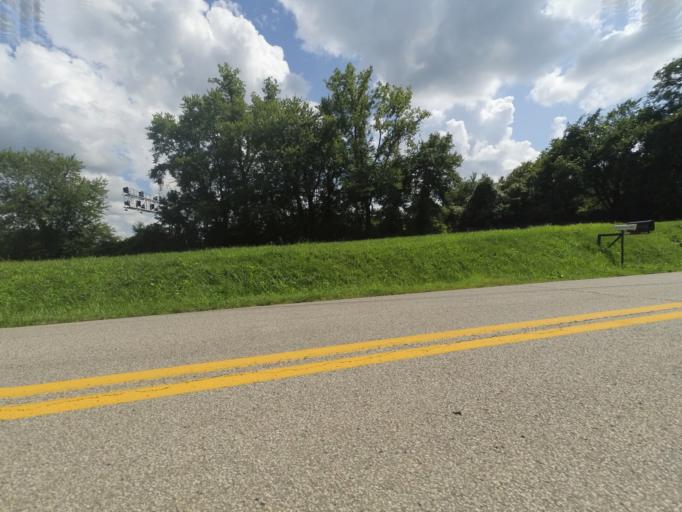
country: US
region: West Virginia
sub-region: Cabell County
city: Pea Ridge
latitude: 38.4192
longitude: -82.3537
